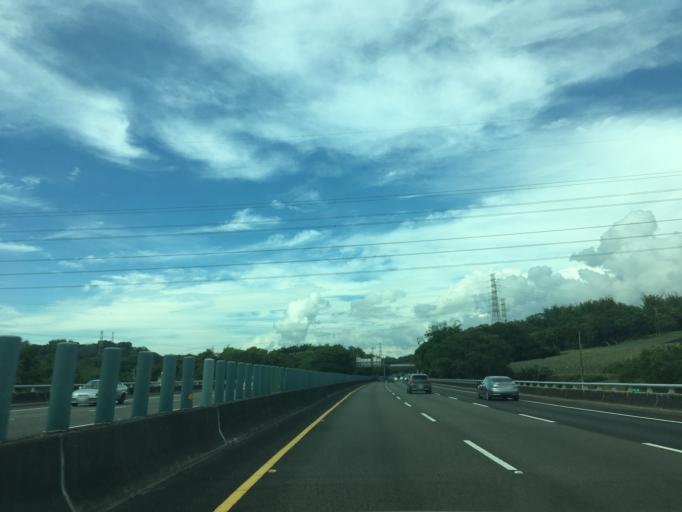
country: TW
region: Taiwan
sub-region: Chiayi
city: Jiayi Shi
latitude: 23.5371
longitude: 120.4933
